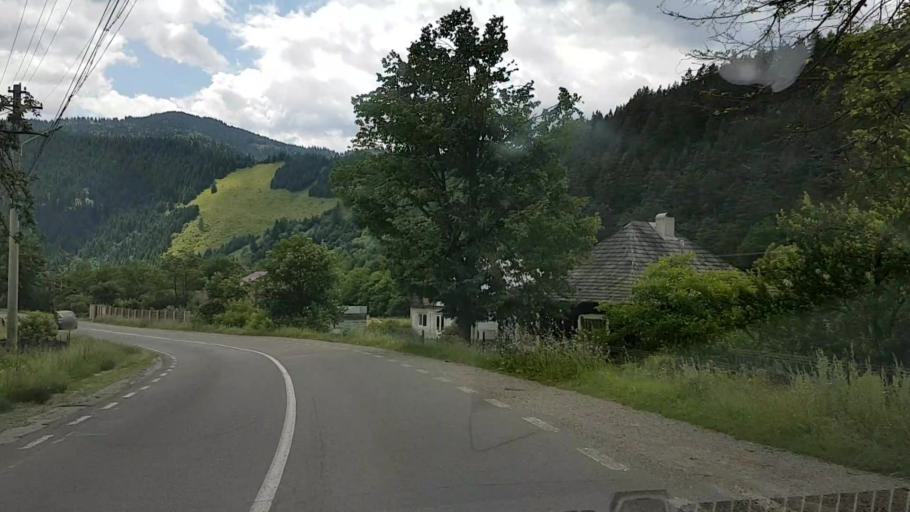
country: RO
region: Suceava
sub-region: Comuna Brosteni
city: Brosteni
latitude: 47.2285
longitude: 25.7435
